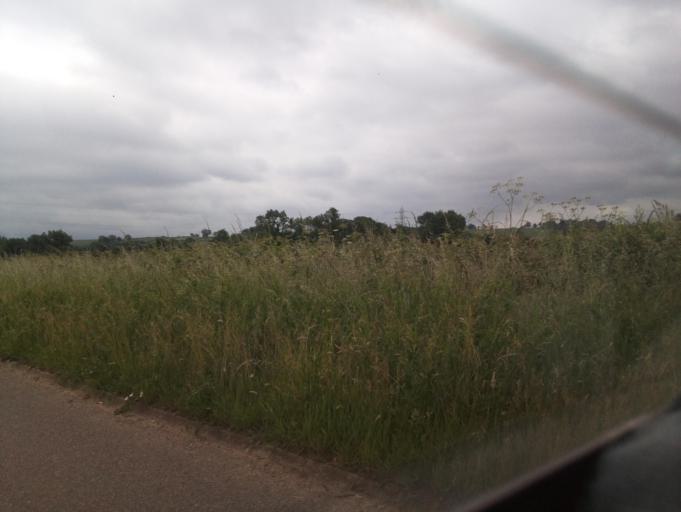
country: GB
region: England
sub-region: District of Rutland
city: Oakham
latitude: 52.6626
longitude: -0.7226
